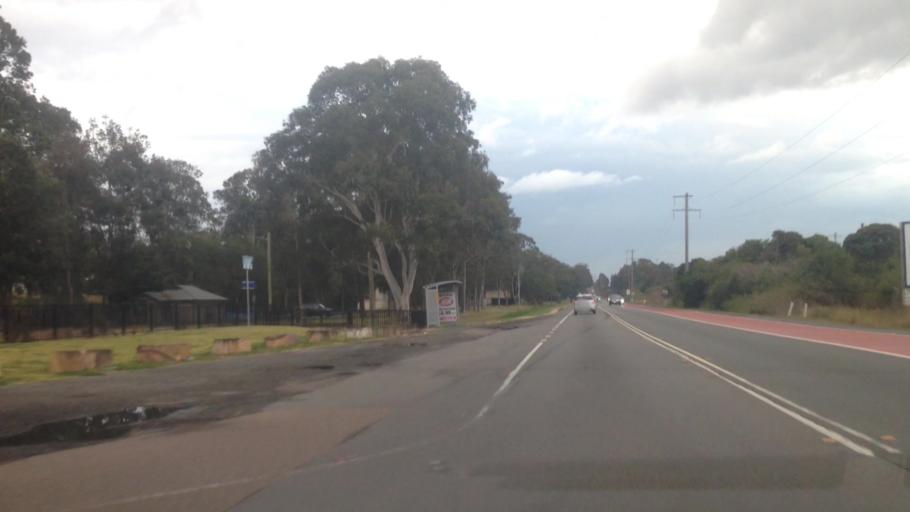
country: AU
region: New South Wales
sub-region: Wyong Shire
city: Chittaway Bay
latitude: -33.2805
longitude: 151.4266
